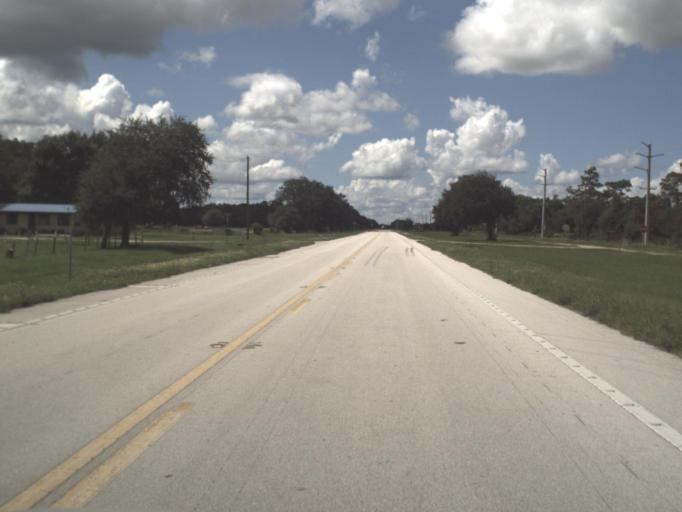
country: US
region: Florida
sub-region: DeSoto County
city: Southeast Arcadia
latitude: 27.2087
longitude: -81.7605
